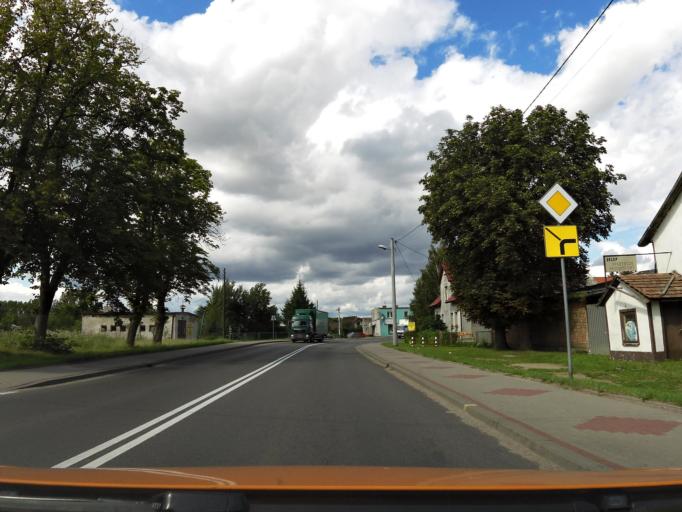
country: PL
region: West Pomeranian Voivodeship
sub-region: Powiat goleniowski
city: Nowogard
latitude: 53.7212
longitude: 15.1896
